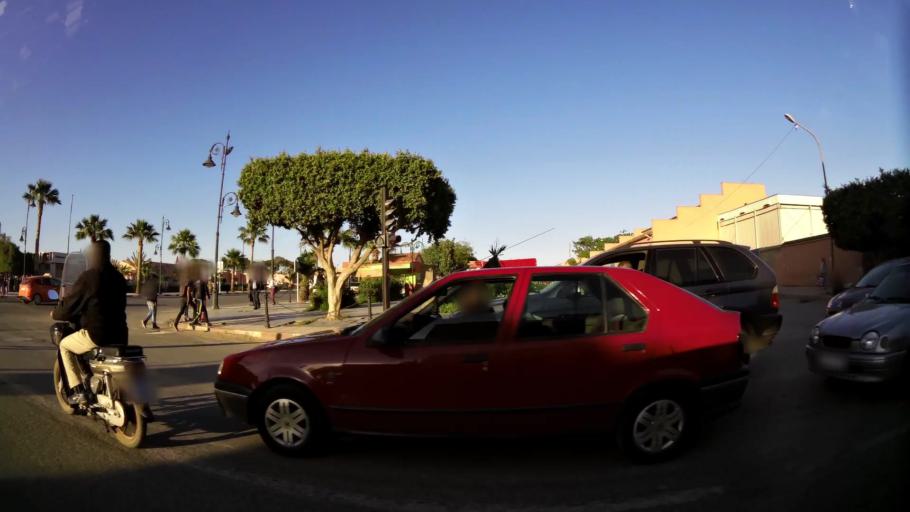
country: MA
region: Oriental
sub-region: Berkane-Taourirt
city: Berkane
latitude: 34.9290
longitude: -2.3188
